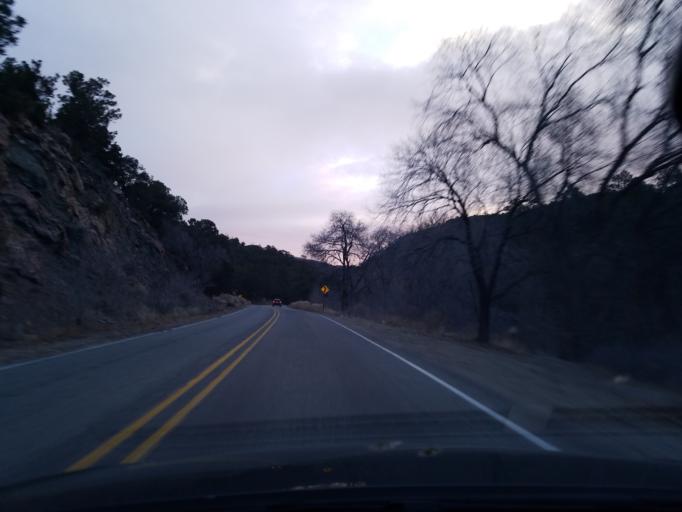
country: US
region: New Mexico
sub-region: Santa Fe County
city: Santa Fe
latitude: 35.7262
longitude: -105.8862
